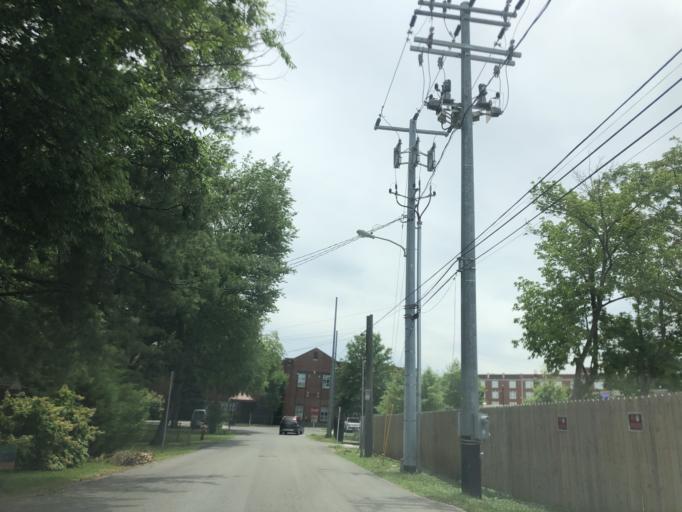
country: US
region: Tennessee
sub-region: Davidson County
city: Oak Hill
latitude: 36.1078
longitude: -86.7969
